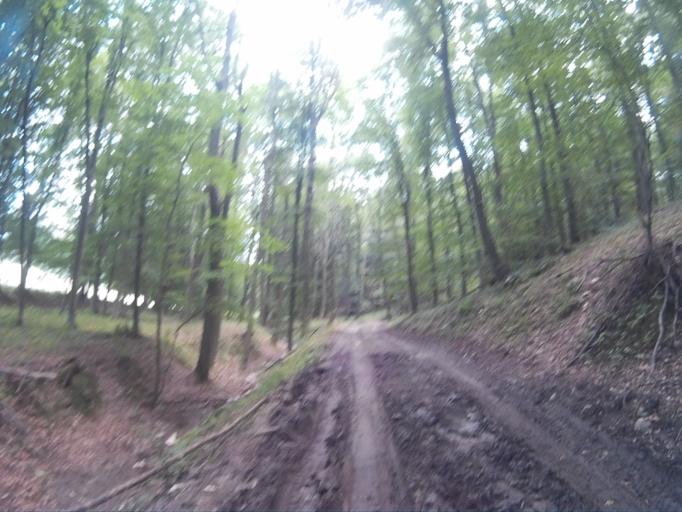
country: HU
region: Veszprem
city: Zirc
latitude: 47.1993
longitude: 17.9139
